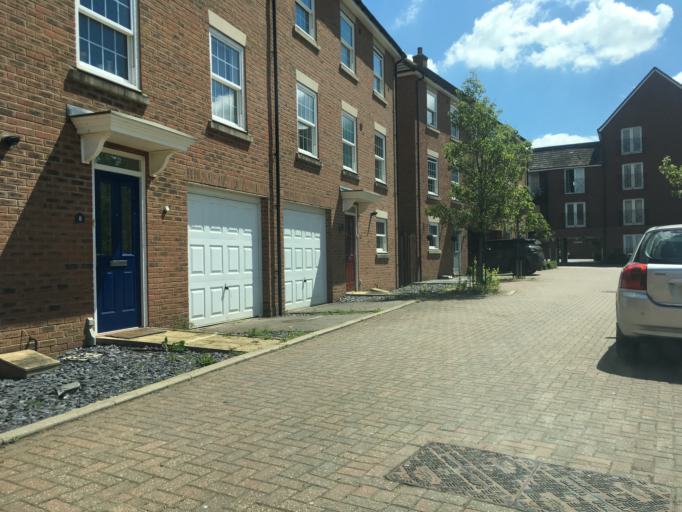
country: GB
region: England
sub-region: Milton Keynes
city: Woburn Sands
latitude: 52.0168
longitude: -0.6531
